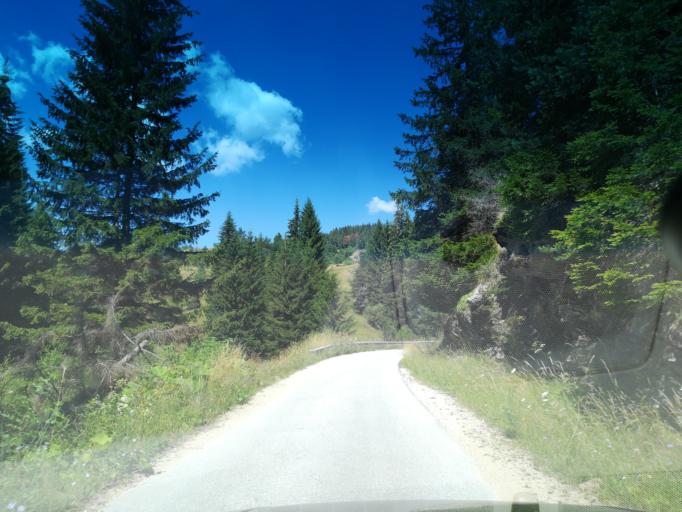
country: BG
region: Smolyan
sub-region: Obshtina Chepelare
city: Chepelare
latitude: 41.6700
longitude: 24.7941
